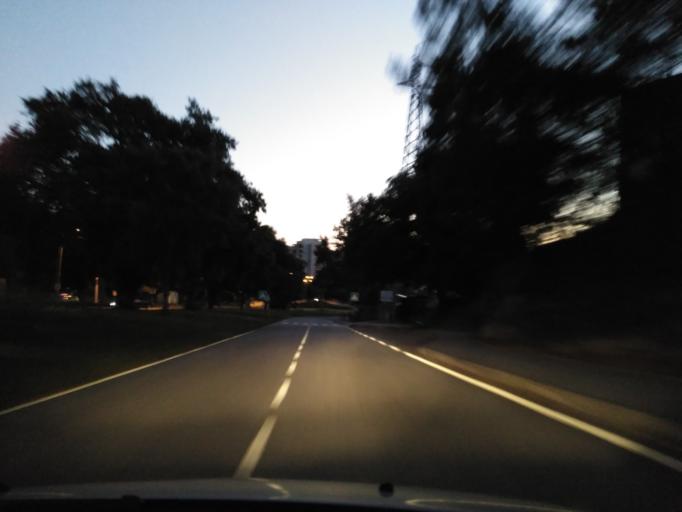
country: PT
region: Braga
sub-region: Braga
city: Braga
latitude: 41.5572
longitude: -8.3938
